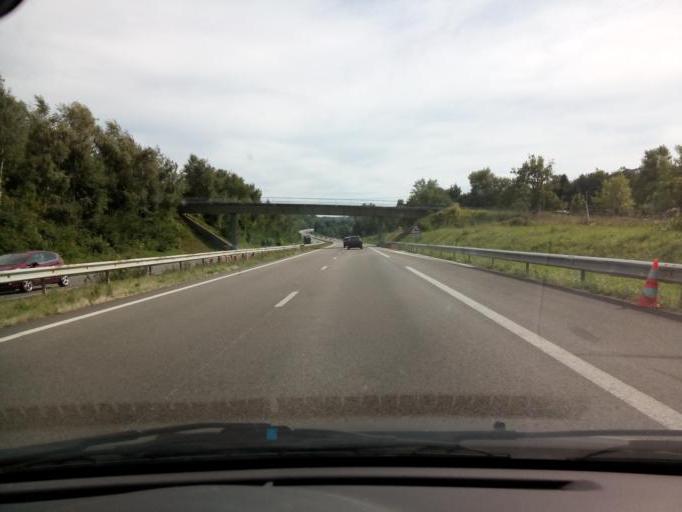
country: FR
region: Rhone-Alpes
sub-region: Departement de l'Isere
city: Chabons
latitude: 45.4766
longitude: 5.3986
